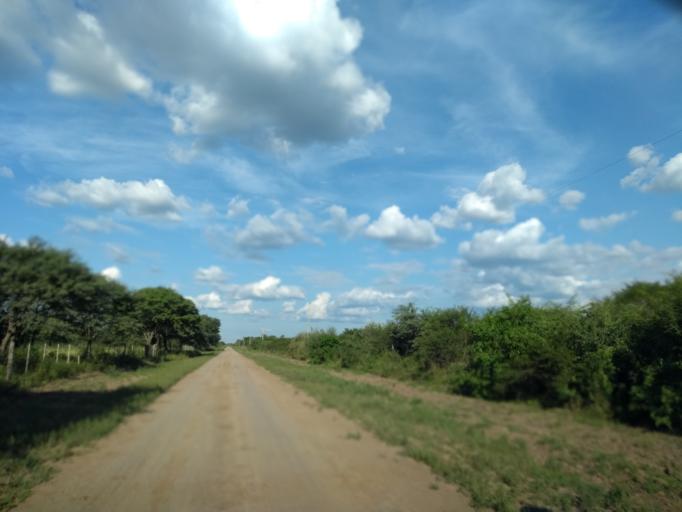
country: AR
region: Chaco
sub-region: Departamento de Quitilipi
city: Quitilipi
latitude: -26.7704
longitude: -60.2051
